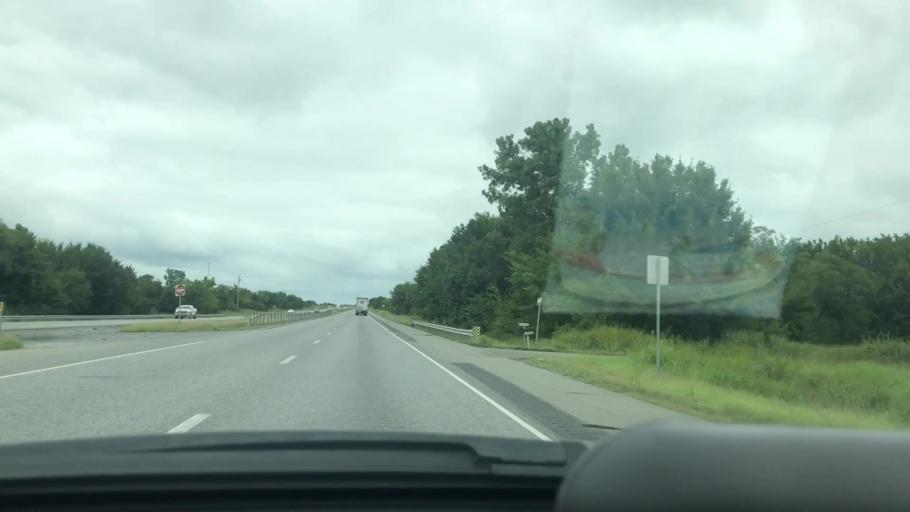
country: US
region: Oklahoma
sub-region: Pittsburg County
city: McAlester
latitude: 34.7411
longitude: -95.8978
